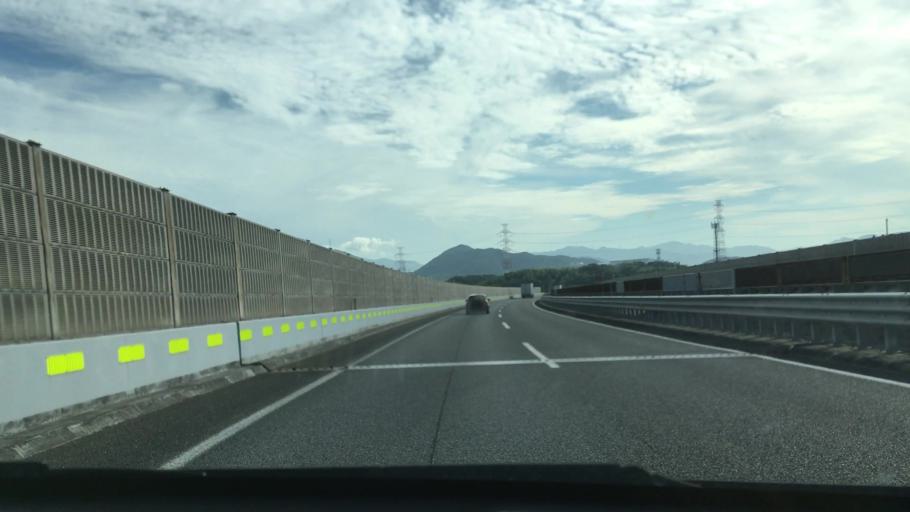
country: JP
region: Fukuoka
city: Kanda
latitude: 33.8361
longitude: 130.9224
